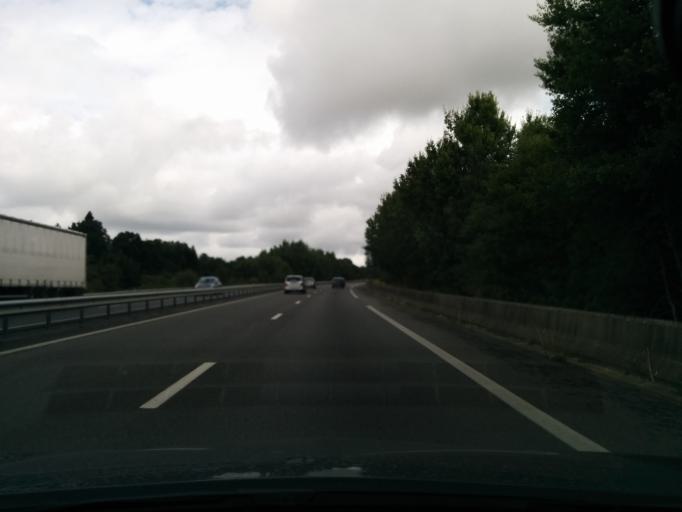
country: FR
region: Limousin
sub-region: Departement de la Correze
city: Uzerche
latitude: 45.4528
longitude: 1.5088
